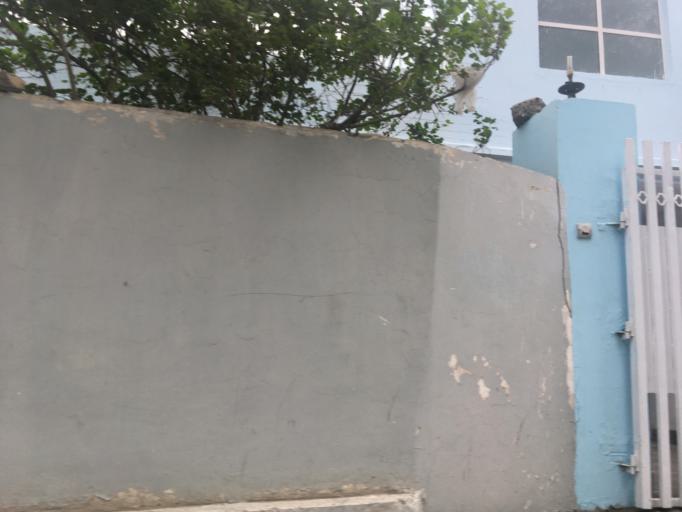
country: PK
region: Gilgit-Baltistan
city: Skardu
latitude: 35.2767
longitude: 75.6370
